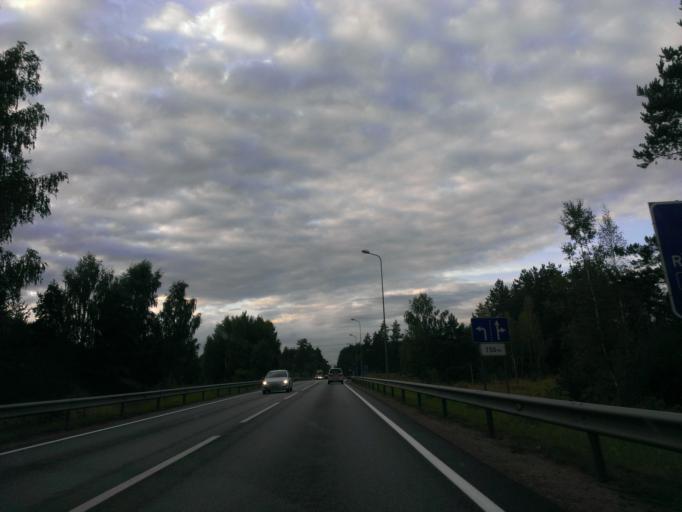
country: LV
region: Salaspils
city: Salaspils
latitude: 56.9405
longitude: 24.3836
